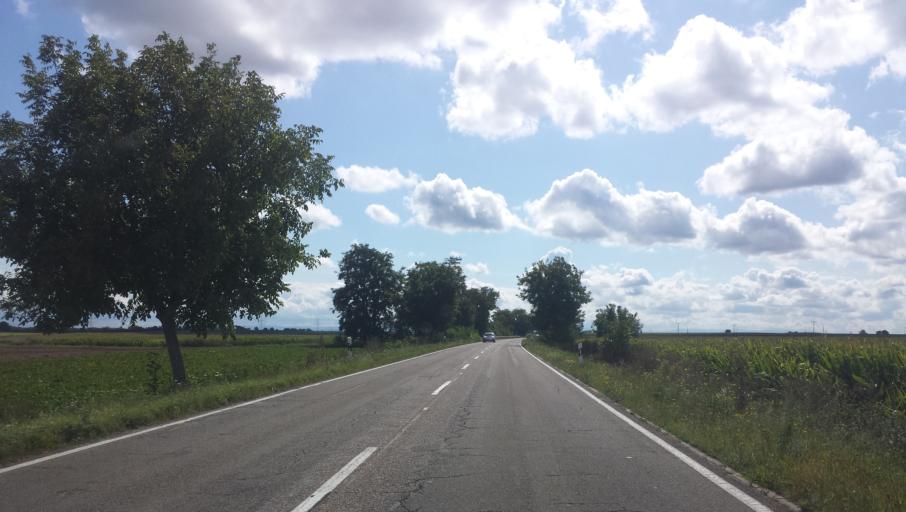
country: DE
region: Rheinland-Pfalz
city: Bellheim
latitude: 49.1847
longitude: 8.2843
